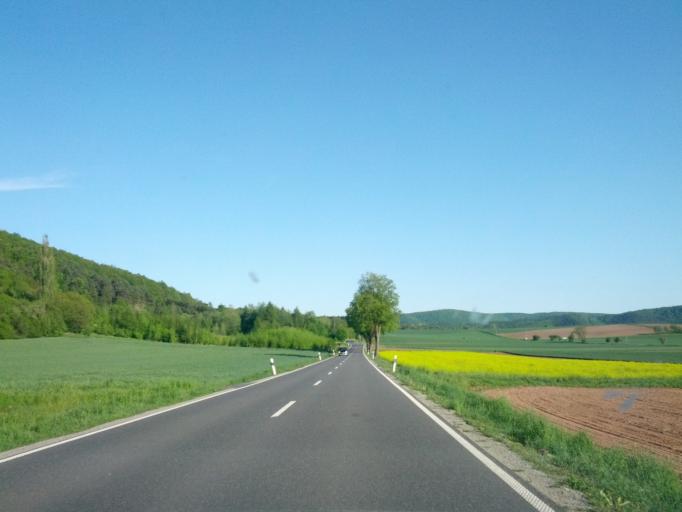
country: DE
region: Hesse
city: Wanfried
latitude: 51.1499
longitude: 10.1890
